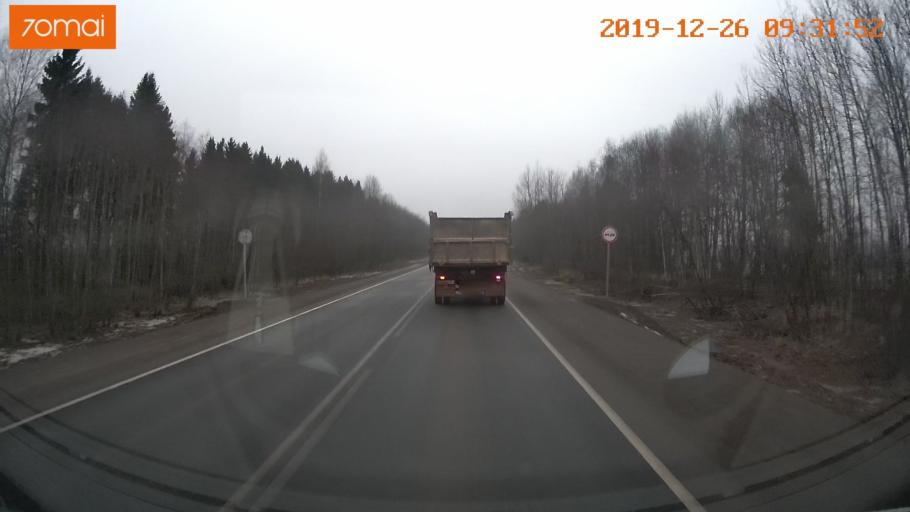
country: RU
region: Vologda
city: Gryazovets
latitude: 59.0728
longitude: 40.1231
